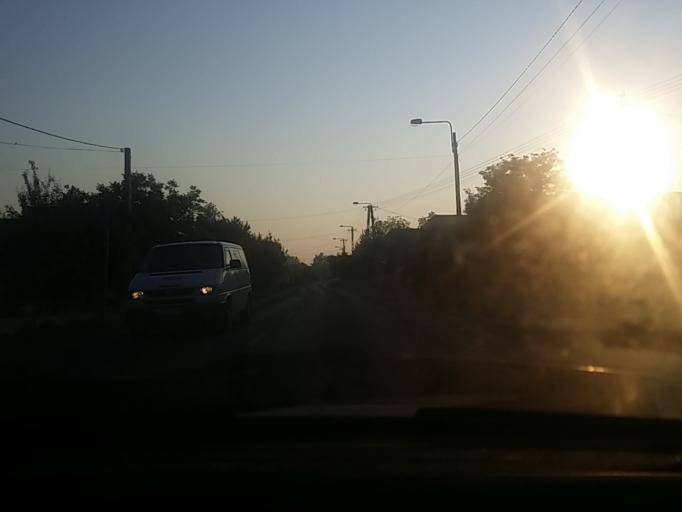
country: HU
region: Pest
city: Szentmartonkata
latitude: 47.4512
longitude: 19.6971
